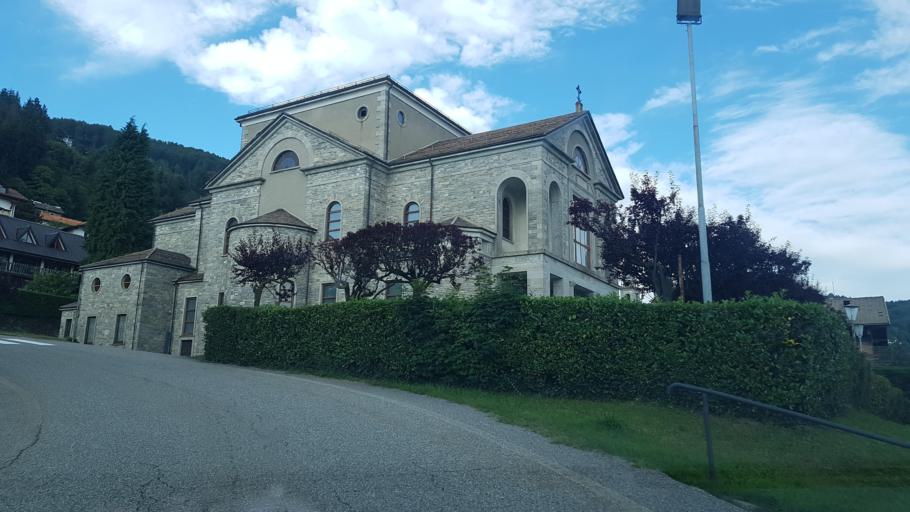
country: IT
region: Piedmont
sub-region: Provincia Verbano-Cusio-Ossola
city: Premeno
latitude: 45.9757
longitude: 8.5928
